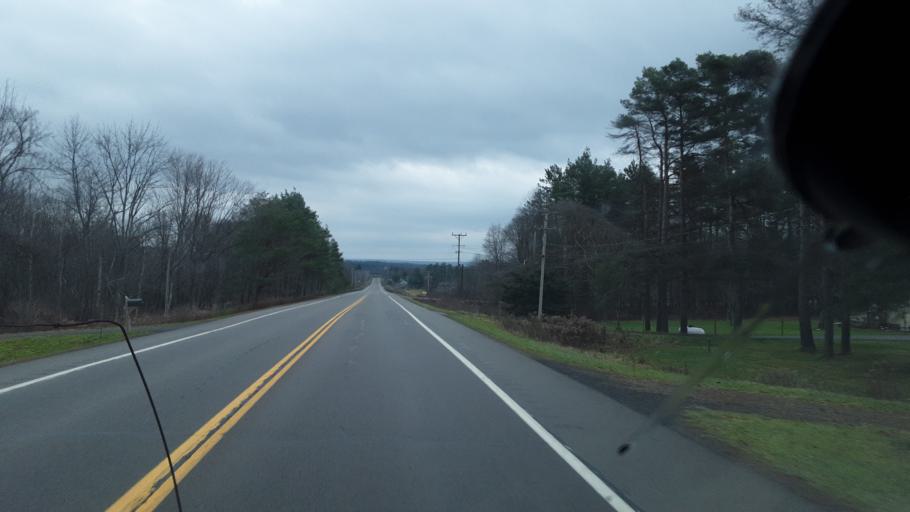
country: US
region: New York
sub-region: Allegany County
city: Houghton
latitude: 42.3893
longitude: -78.2242
